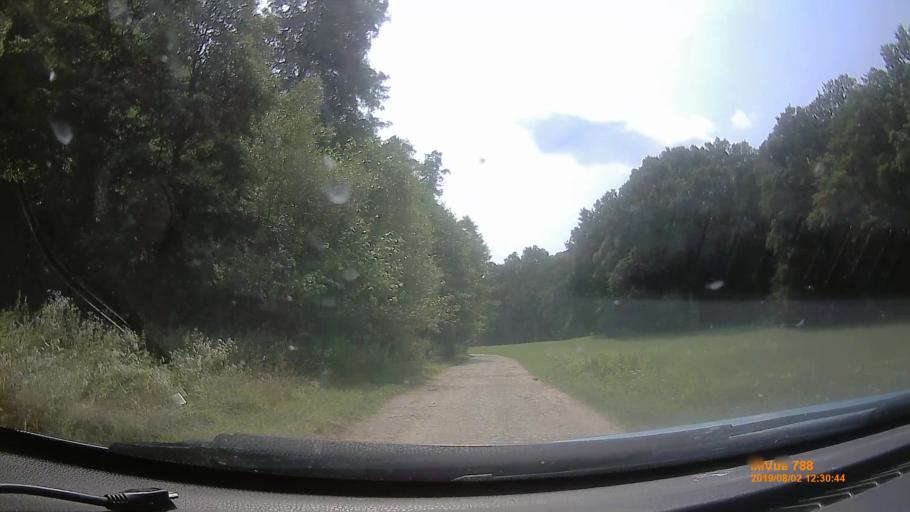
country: HU
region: Baranya
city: Buekkoesd
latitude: 46.1080
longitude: 17.9355
